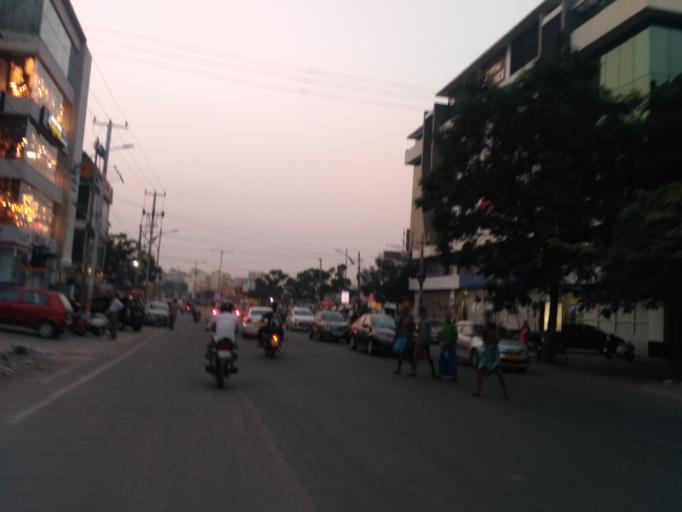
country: IN
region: Telangana
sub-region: Rangareddi
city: Kukatpalli
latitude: 17.4421
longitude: 78.3964
